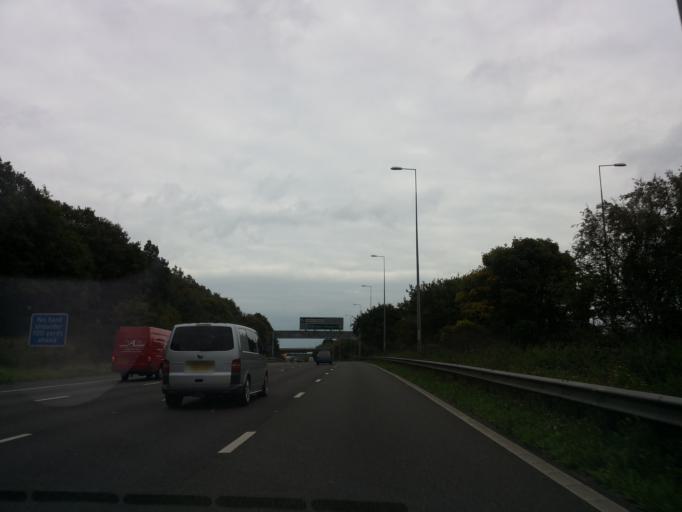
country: GB
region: England
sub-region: Medway
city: Cuxton
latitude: 51.4014
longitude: 0.4130
